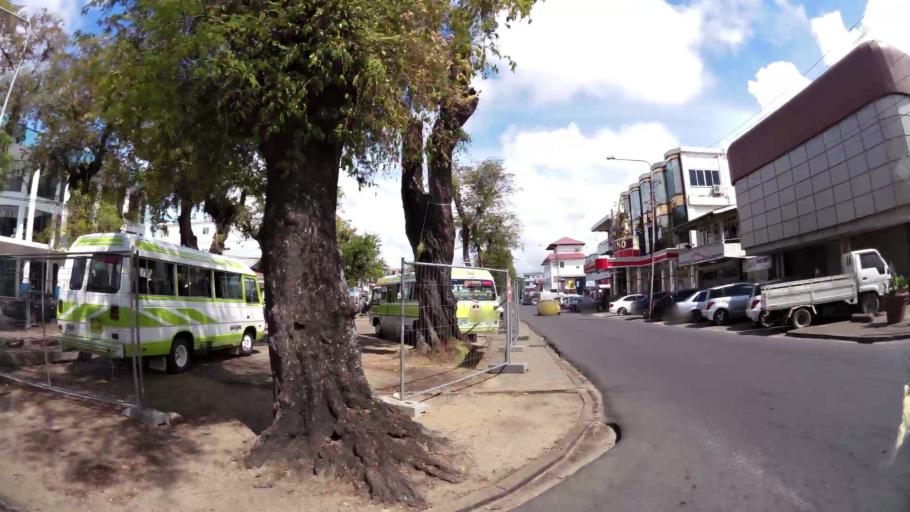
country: SR
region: Paramaribo
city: Paramaribo
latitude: 5.8258
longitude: -55.1640
